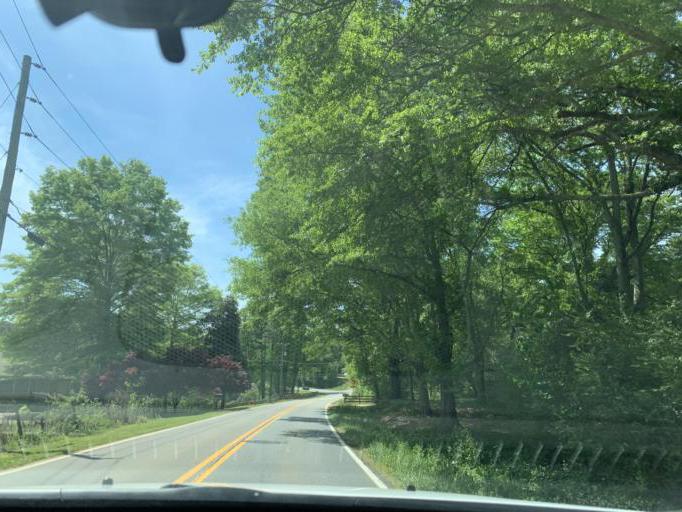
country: US
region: Georgia
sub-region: Forsyth County
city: Cumming
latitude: 34.2735
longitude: -84.2042
